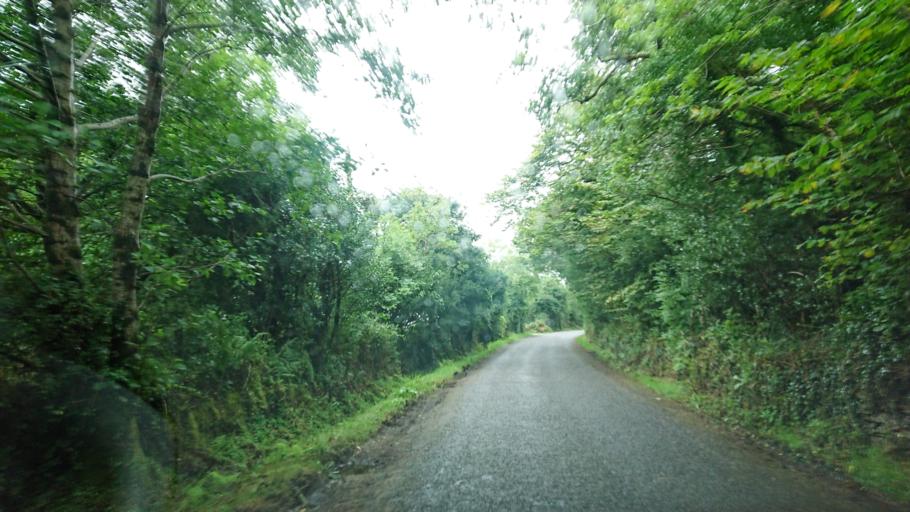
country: IE
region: Munster
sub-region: Ciarrai
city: Cahersiveen
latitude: 52.0190
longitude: -10.0980
